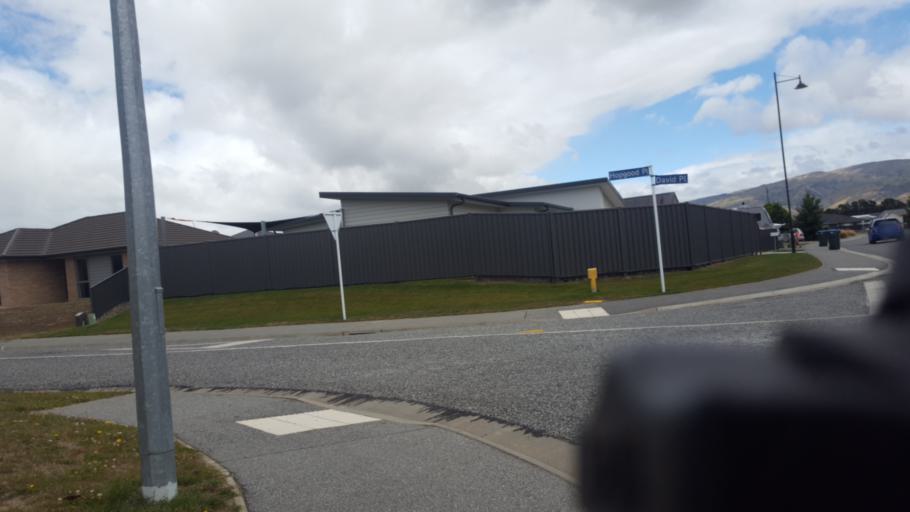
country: NZ
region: Otago
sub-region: Queenstown-Lakes District
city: Wanaka
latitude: -45.0458
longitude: 169.1809
